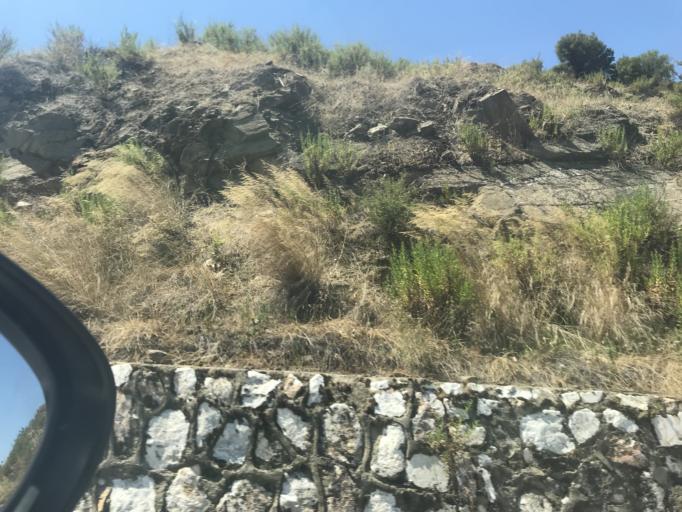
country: TR
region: Aydin
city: Akcaova
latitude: 37.5100
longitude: 28.1003
